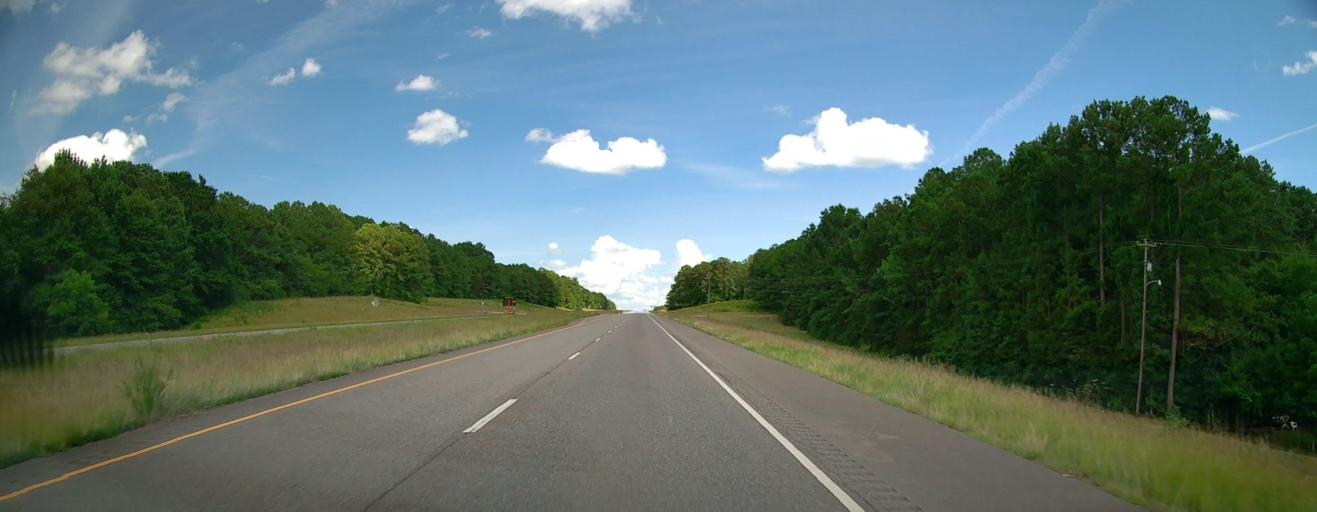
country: US
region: Alabama
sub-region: Pickens County
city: Reform
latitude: 33.3997
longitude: -88.0650
